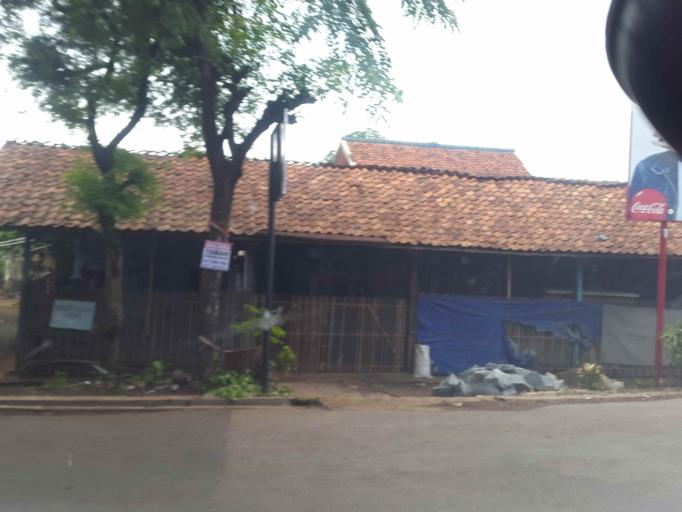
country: ID
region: West Java
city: Cileungsir
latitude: -6.3616
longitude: 106.9341
